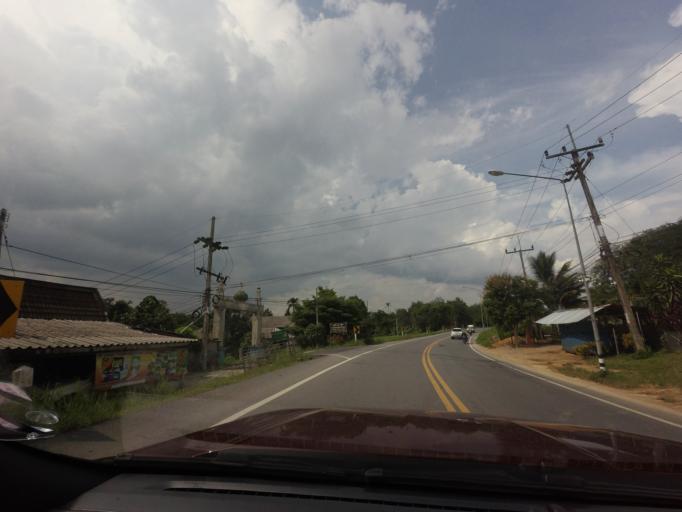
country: TH
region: Yala
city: Ban Nang Sata
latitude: 6.2555
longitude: 101.2343
